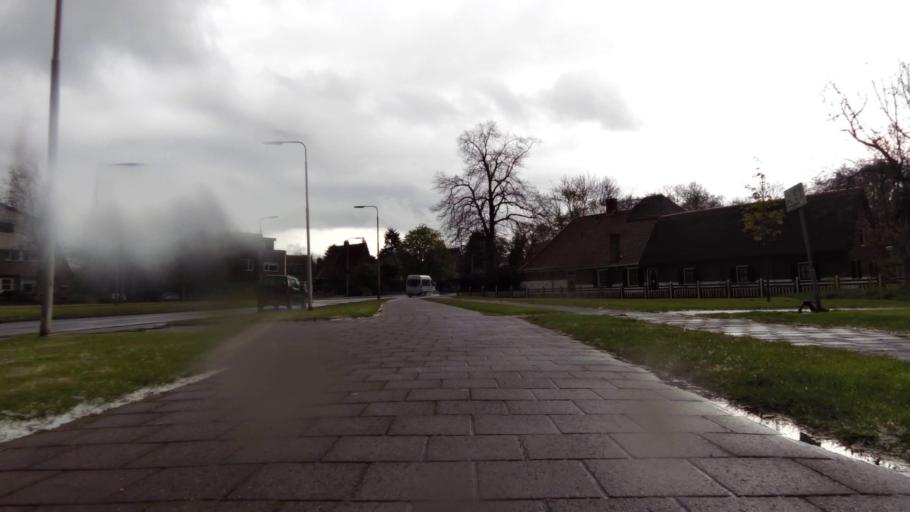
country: NL
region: North Holland
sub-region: Gemeente Velsen
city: Velsen-Zuid
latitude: 52.4525
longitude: 4.6287
